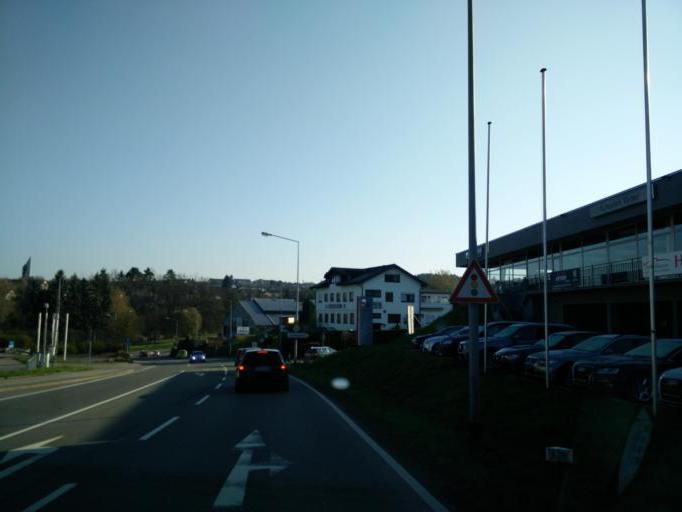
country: DE
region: Baden-Wuerttemberg
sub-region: Karlsruhe Region
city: Calw
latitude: 48.7062
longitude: 8.7623
